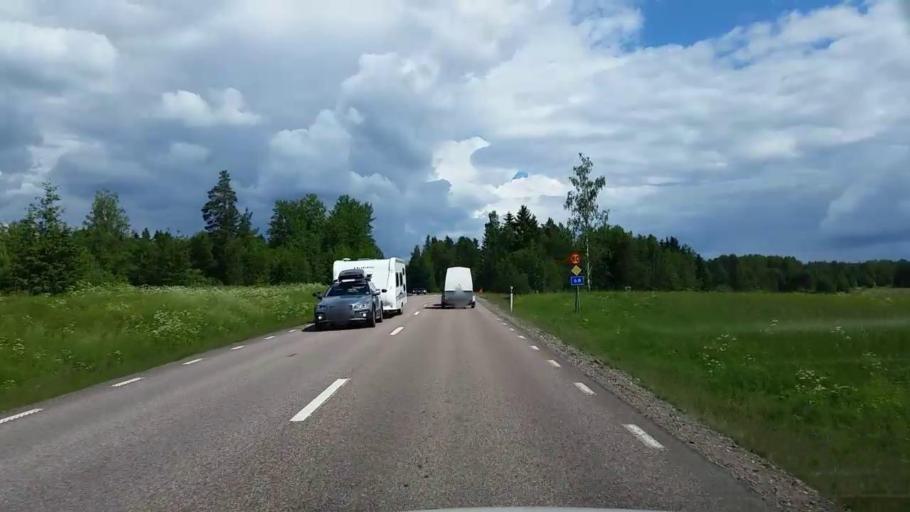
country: SE
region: Dalarna
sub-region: Avesta Kommun
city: Avesta
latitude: 60.1663
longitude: 16.2751
